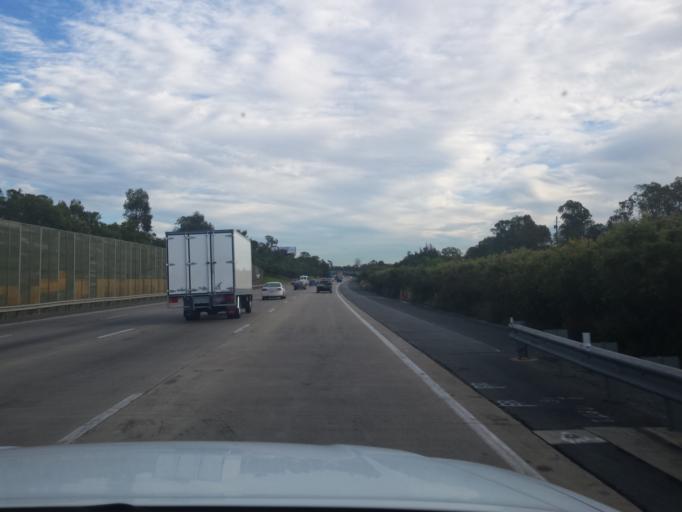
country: AU
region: Queensland
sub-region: Gold Coast
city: Ormeau Hills
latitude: -27.7983
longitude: 153.2612
